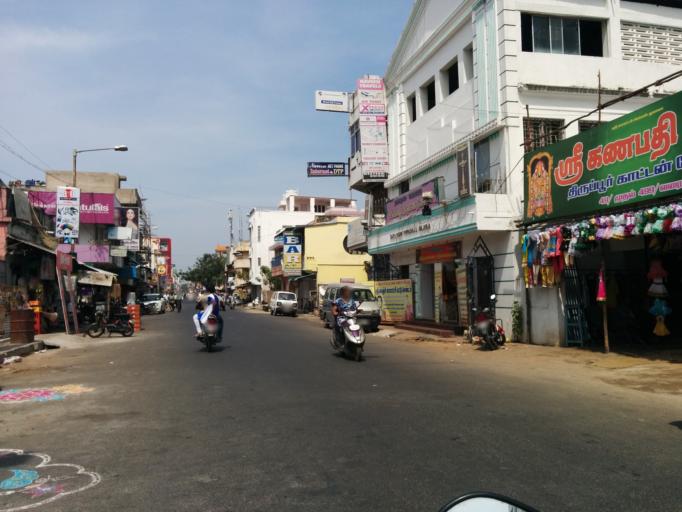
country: IN
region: Pondicherry
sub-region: Puducherry
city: Puducherry
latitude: 11.9305
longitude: 79.8283
